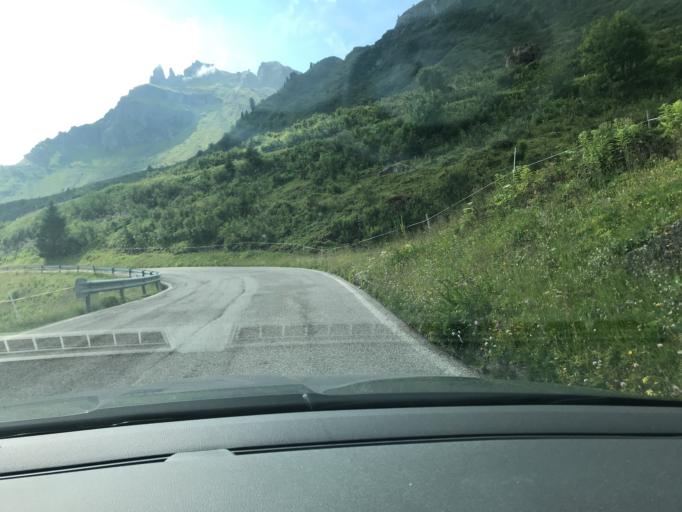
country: IT
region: Trentino-Alto Adige
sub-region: Provincia di Trento
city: Canazei
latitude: 46.4854
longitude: 11.8393
